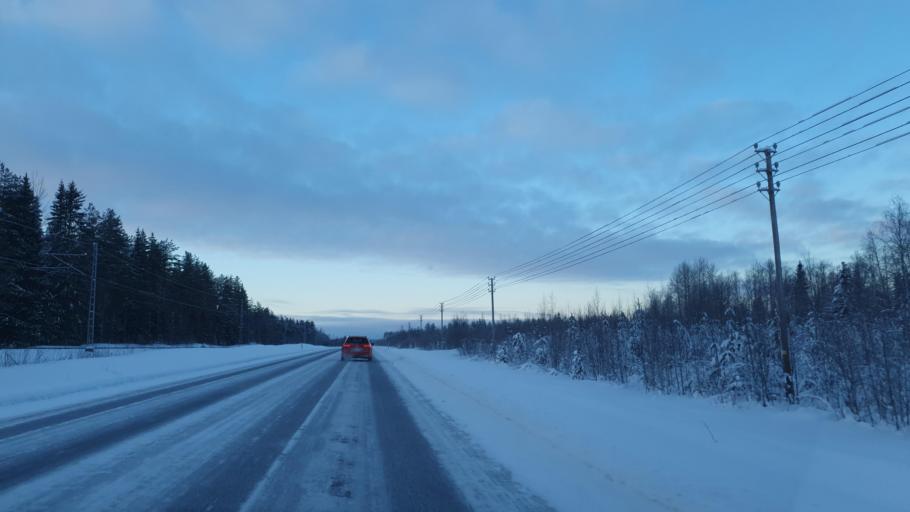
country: FI
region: Kainuu
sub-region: Kajaani
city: Paltamo
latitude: 64.4109
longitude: 27.7533
